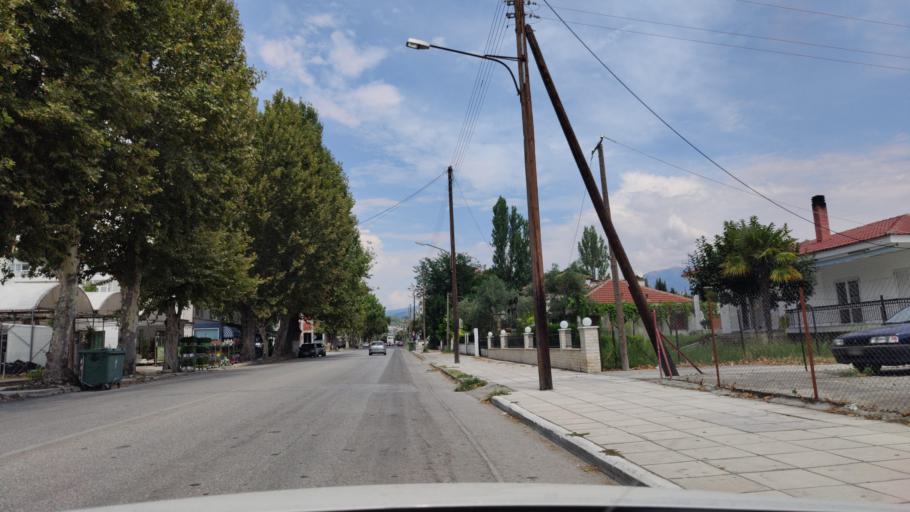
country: GR
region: Central Macedonia
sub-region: Nomos Serron
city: Serres
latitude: 41.0791
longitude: 23.5404
